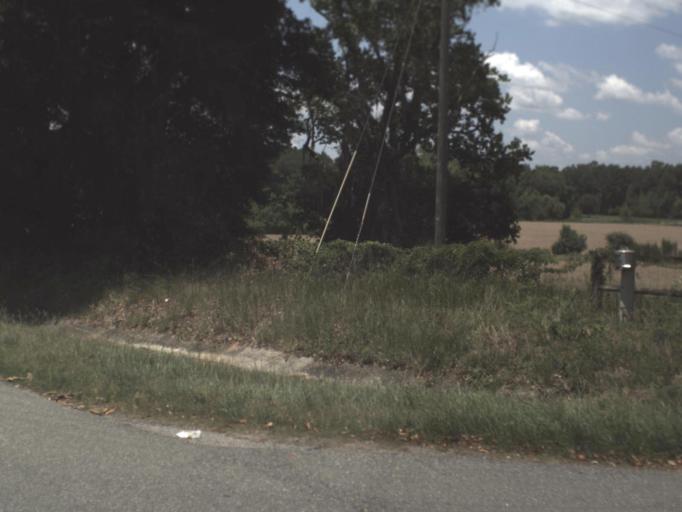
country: US
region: Florida
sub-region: Madison County
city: Madison
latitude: 30.5164
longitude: -83.6330
